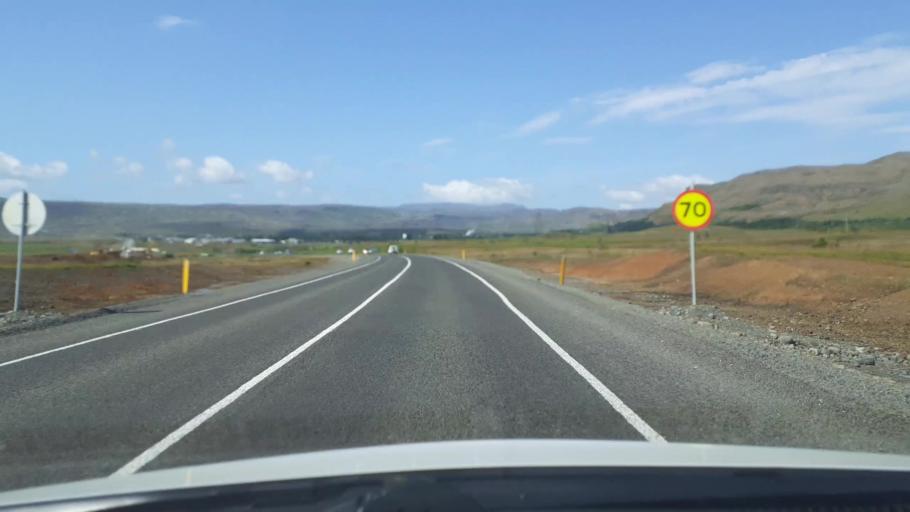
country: IS
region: South
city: Hveragerdi
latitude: 63.9847
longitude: -21.1561
